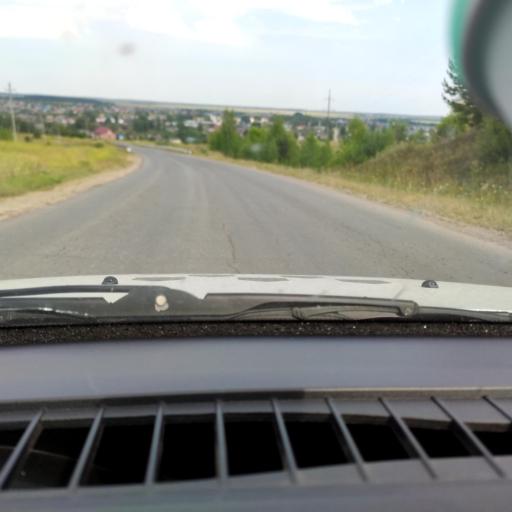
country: RU
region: Perm
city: Orda
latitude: 57.1885
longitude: 56.8840
